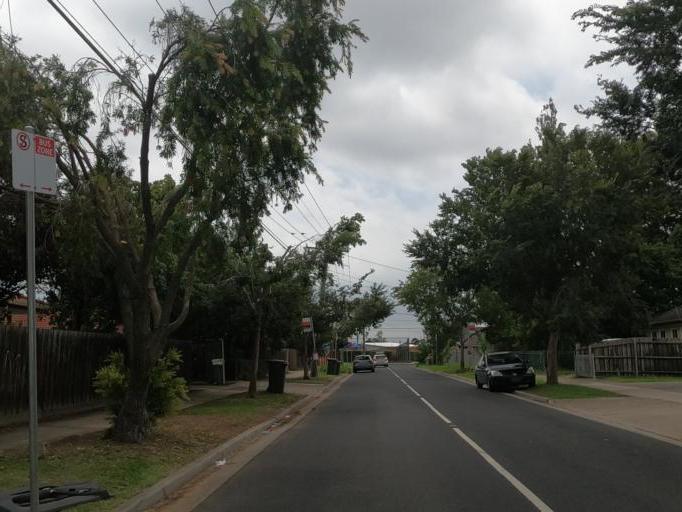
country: AU
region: Victoria
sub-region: Hume
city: Broadmeadows
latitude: -37.6865
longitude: 144.9231
